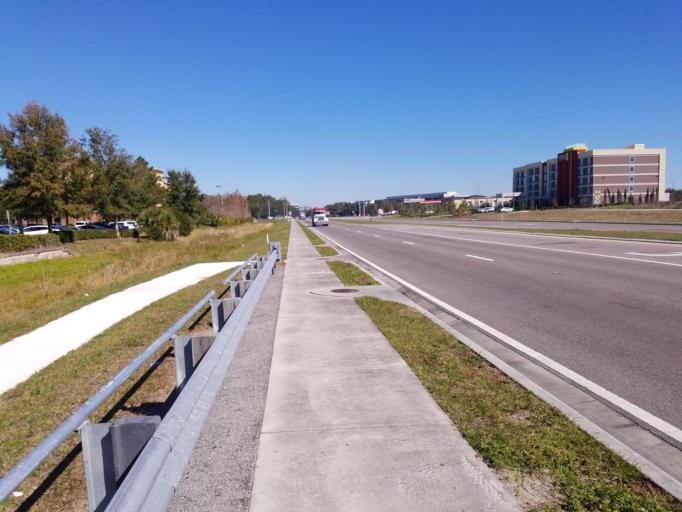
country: US
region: Florida
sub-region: Orange County
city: Tangelo Park
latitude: 28.4376
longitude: -81.4296
